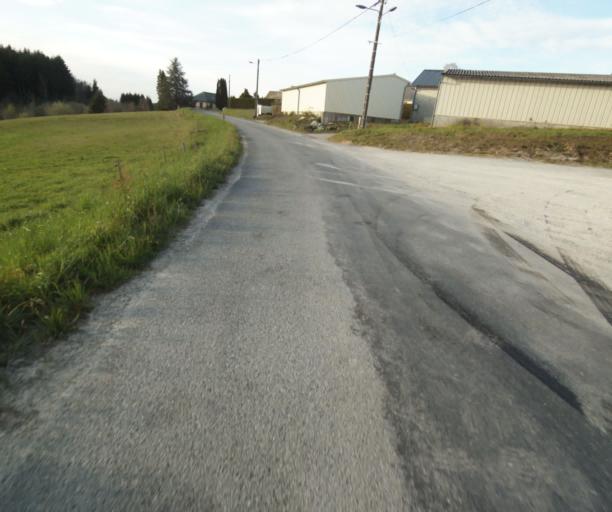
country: FR
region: Limousin
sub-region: Departement de la Correze
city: Correze
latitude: 45.3742
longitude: 1.8656
